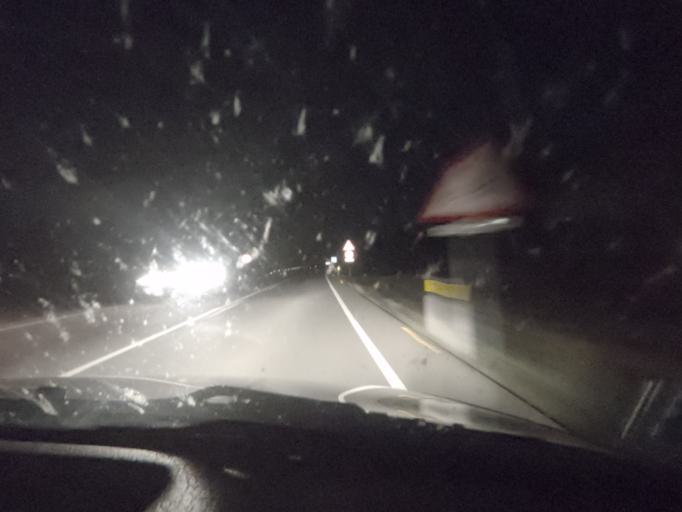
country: ES
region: Extremadura
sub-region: Provincia de Caceres
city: Perales del Puerto
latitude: 40.1252
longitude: -6.6786
